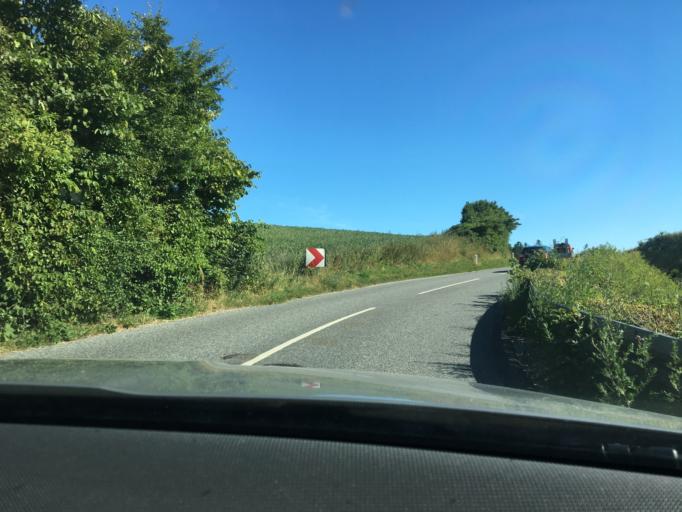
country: DK
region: Central Jutland
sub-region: Syddjurs Kommune
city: Hornslet
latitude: 56.3093
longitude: 10.3433
